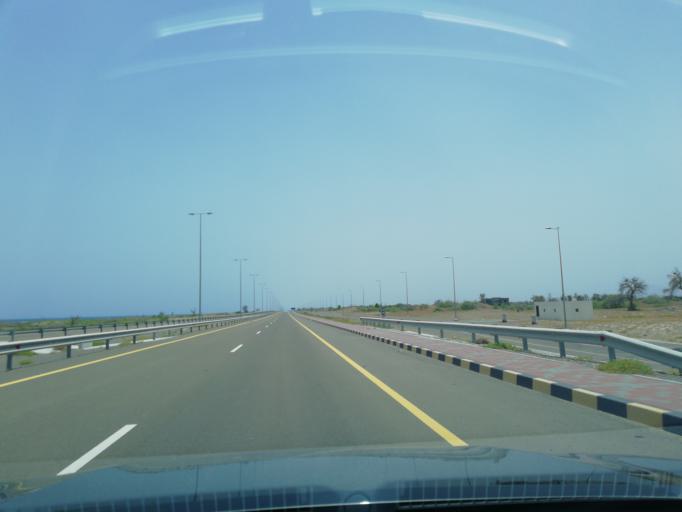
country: OM
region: Al Batinah
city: Shinas
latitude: 24.9119
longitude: 56.3911
